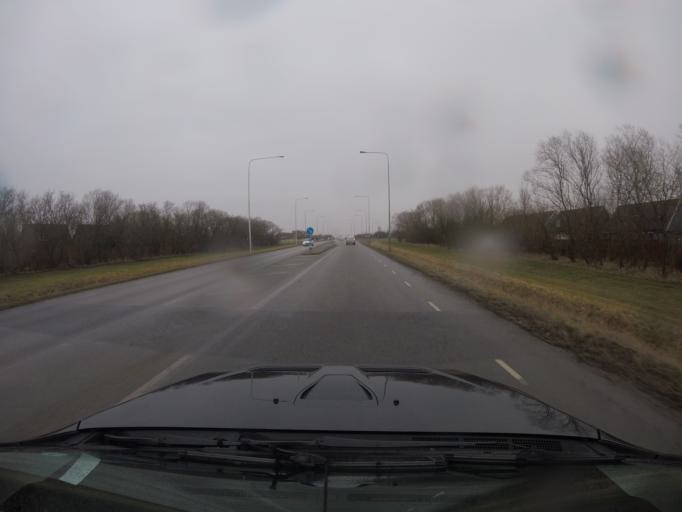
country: SE
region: Skane
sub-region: Trelleborgs Kommun
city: Trelleborg
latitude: 55.3864
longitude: 13.1520
